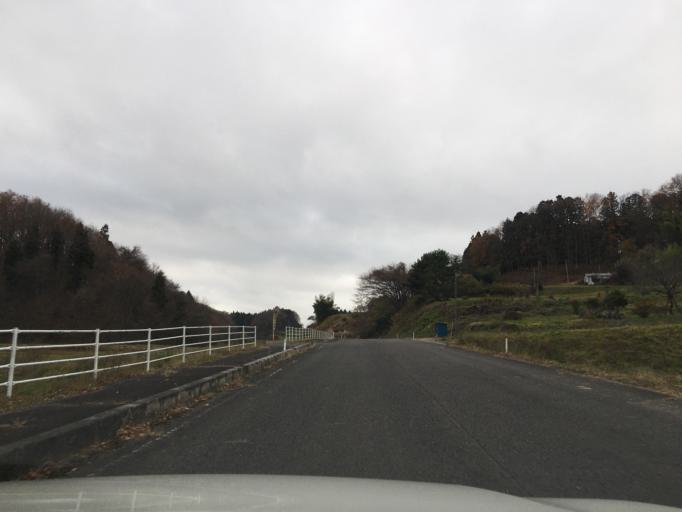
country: JP
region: Fukushima
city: Funehikimachi-funehiki
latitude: 37.4731
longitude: 140.5482
